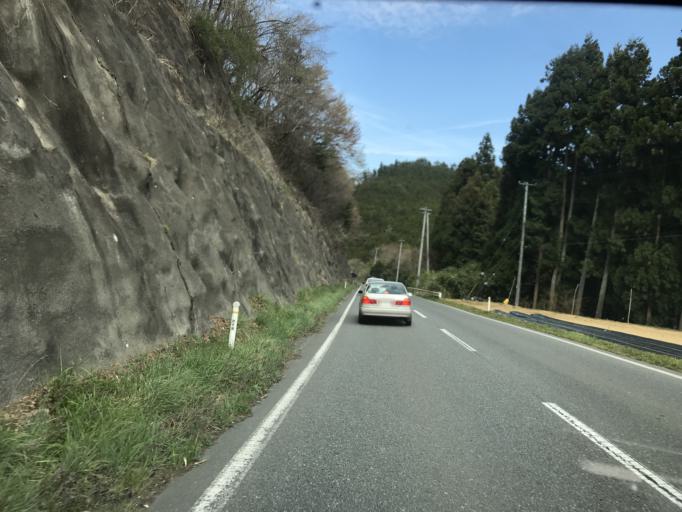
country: JP
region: Iwate
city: Ichinoseki
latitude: 38.8215
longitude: 141.3261
